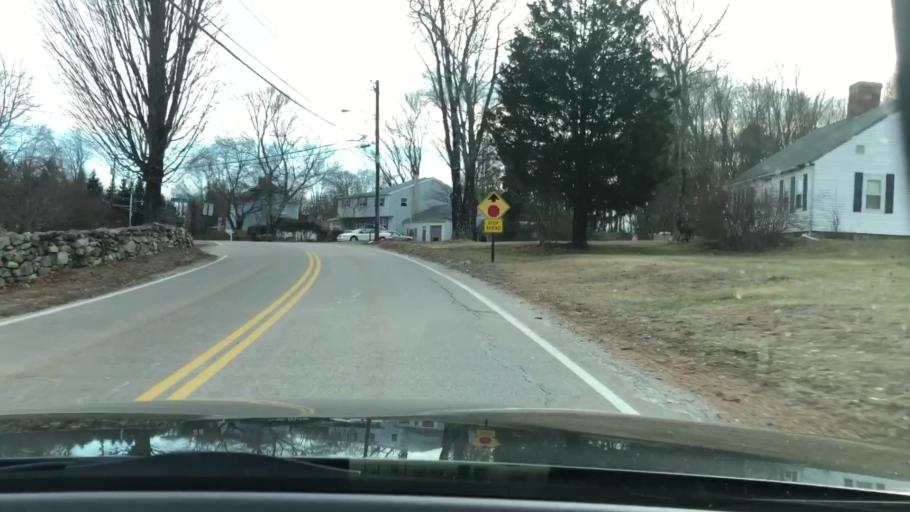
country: US
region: Massachusetts
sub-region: Worcester County
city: Blackstone
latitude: 42.0516
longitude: -71.5327
